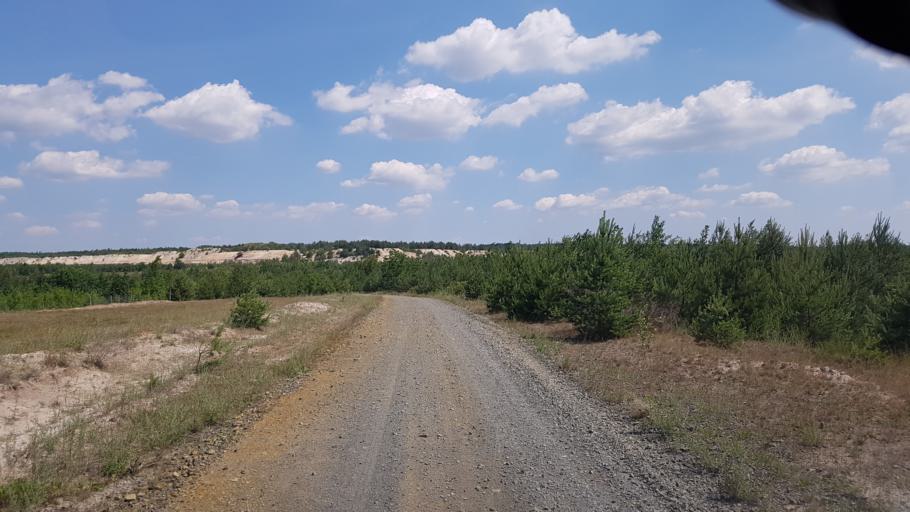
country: DE
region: Brandenburg
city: Sallgast
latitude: 51.5614
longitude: 13.8017
